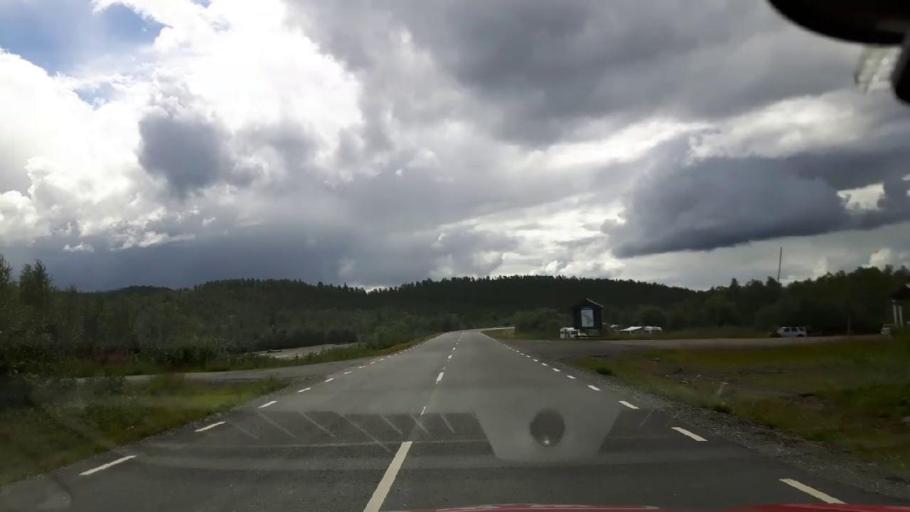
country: NO
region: Nordland
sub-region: Hattfjelldal
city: Hattfjelldal
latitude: 64.9801
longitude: 14.2136
